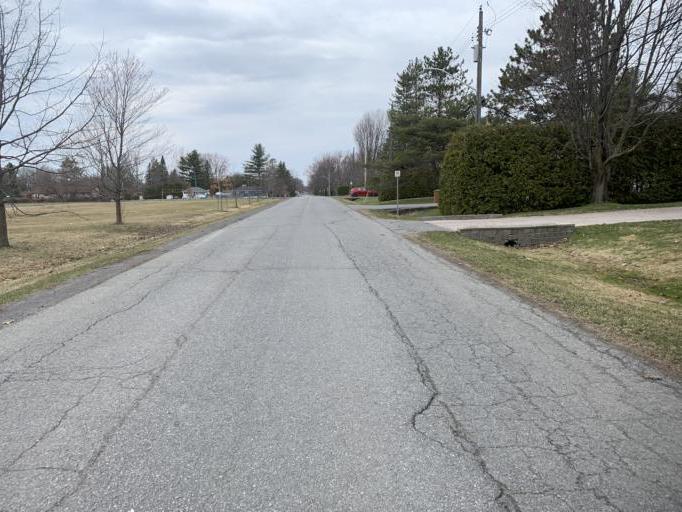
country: CA
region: Ontario
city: Bells Corners
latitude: 45.1877
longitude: -75.8255
